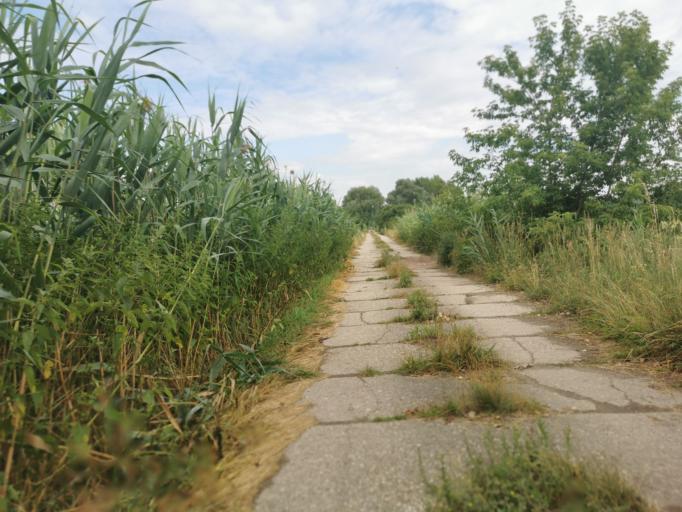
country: CZ
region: South Moravian
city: Tynec
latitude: 48.7655
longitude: 17.0555
